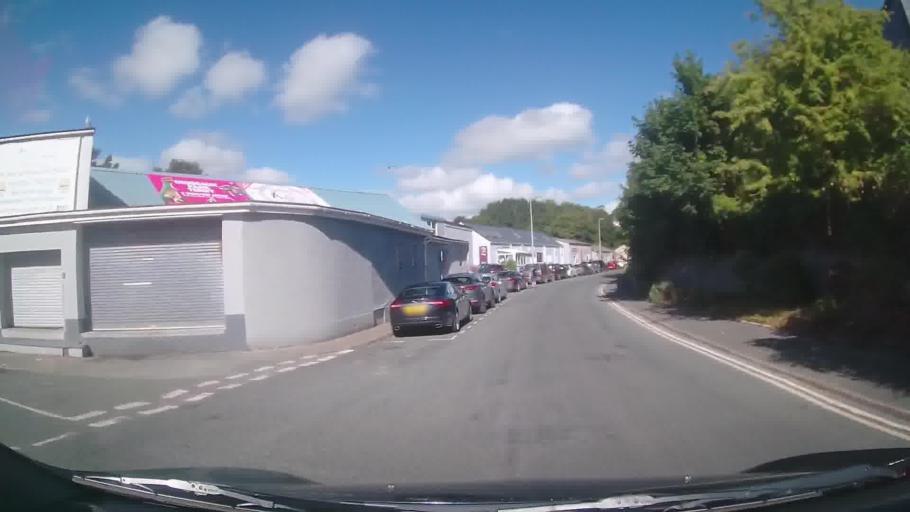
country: GB
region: Wales
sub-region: Pembrokeshire
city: Tenby
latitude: 51.6719
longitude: -4.7073
